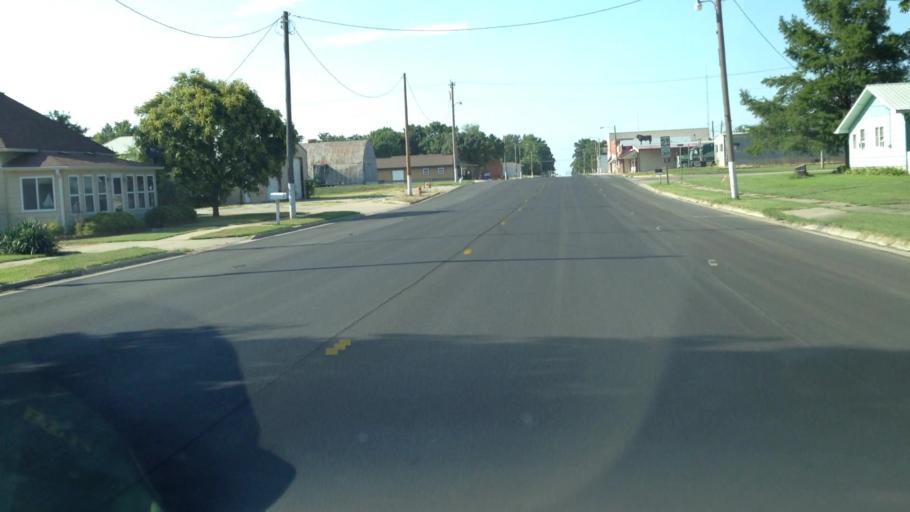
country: US
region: Kansas
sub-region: Allen County
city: Iola
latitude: 37.9133
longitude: -95.1701
